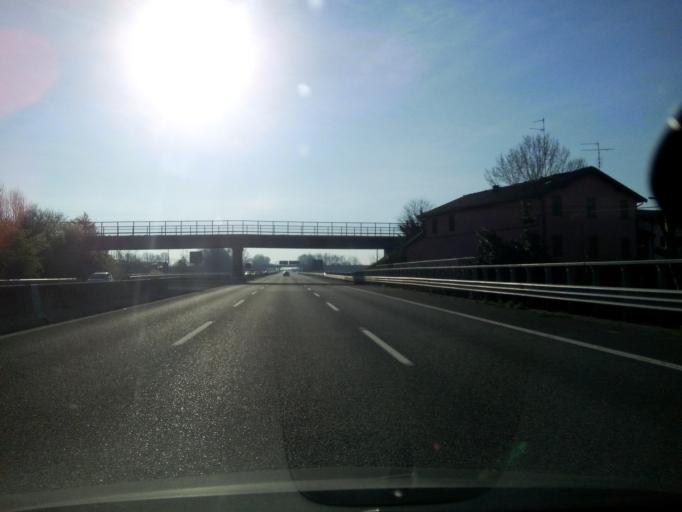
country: IT
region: Emilia-Romagna
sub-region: Provincia di Modena
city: Campogalliano
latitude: 44.6707
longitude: 10.8354
